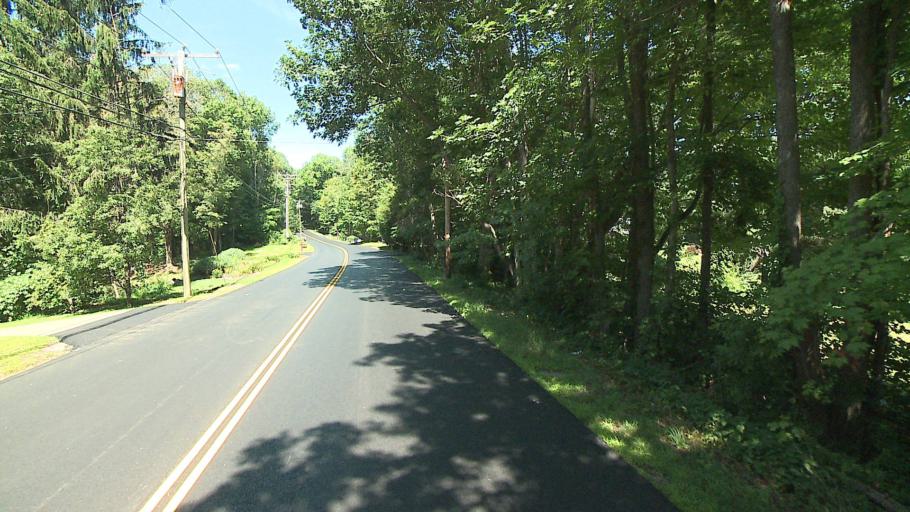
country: US
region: Connecticut
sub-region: Hartford County
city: West Simsbury
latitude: 41.9167
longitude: -72.9031
